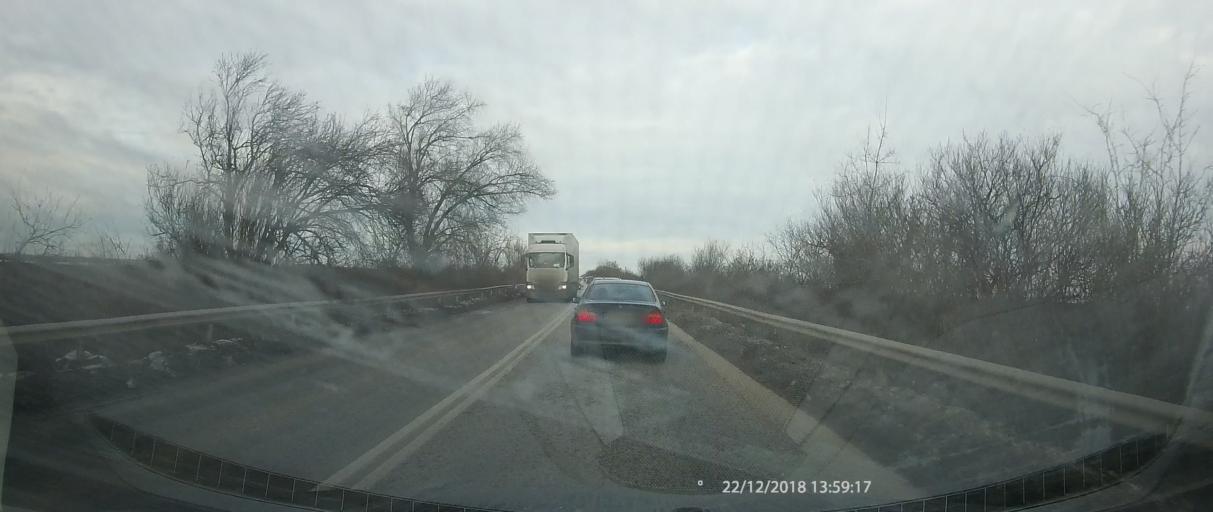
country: BG
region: Pleven
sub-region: Obshtina Dolni Dubnik
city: Dolni Dubnik
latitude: 43.3455
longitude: 24.3439
